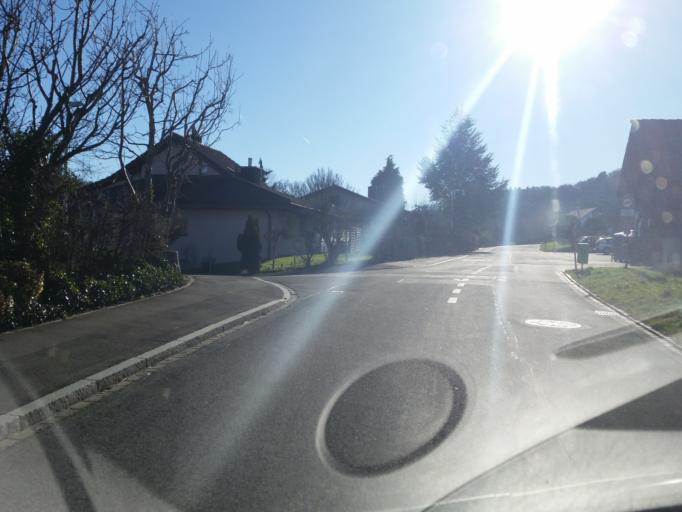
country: CH
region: Zurich
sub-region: Bezirk Dietikon
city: Dietikon / Almend
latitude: 47.3937
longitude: 8.3759
